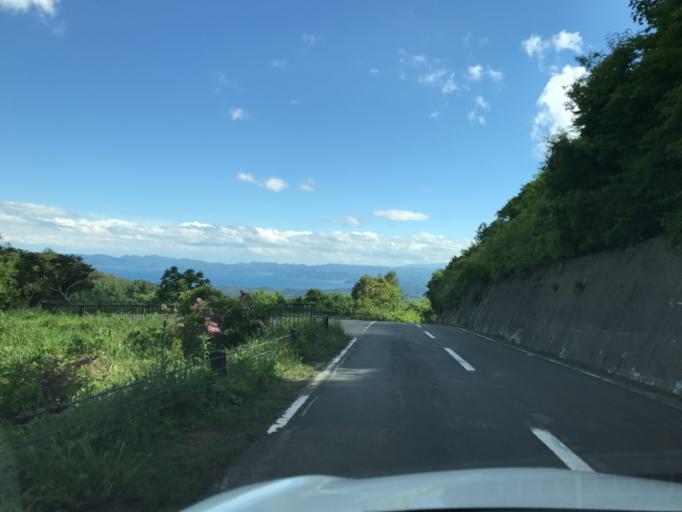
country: JP
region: Fukushima
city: Inawashiro
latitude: 37.5984
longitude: 140.0395
